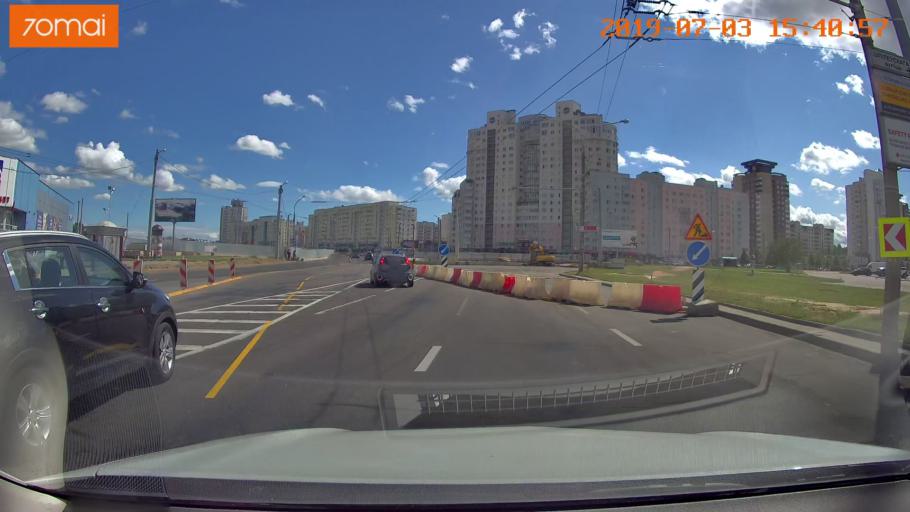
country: BY
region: Minsk
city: Syenitsa
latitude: 53.8470
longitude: 27.5694
